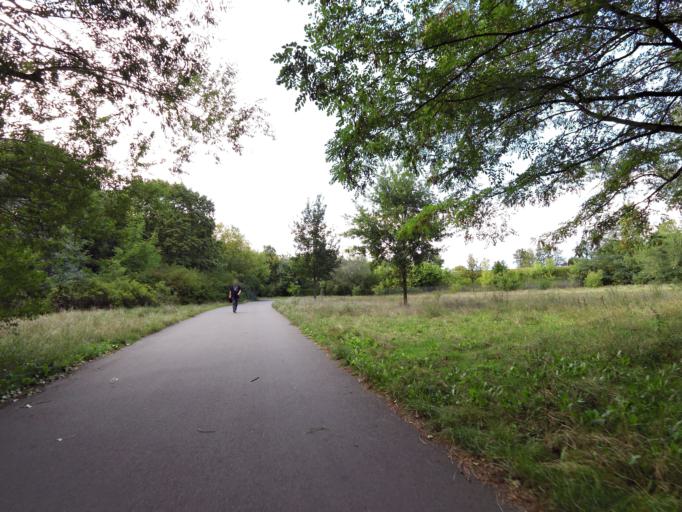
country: DE
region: Berlin
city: Plaenterwald
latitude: 52.4696
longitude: 13.4740
